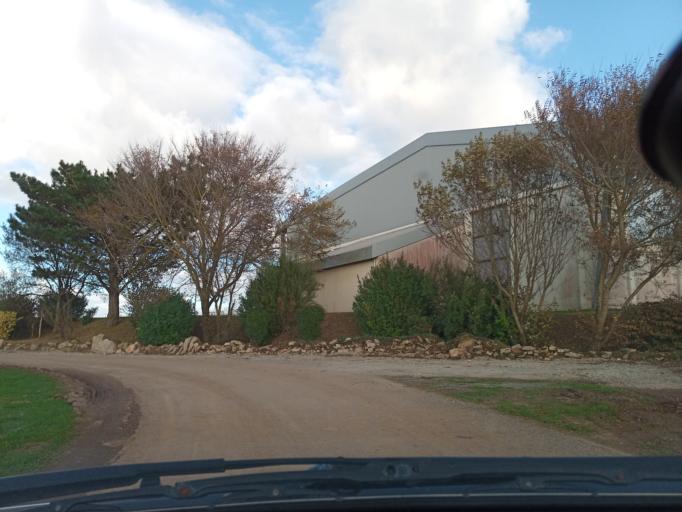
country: FR
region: Brittany
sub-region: Departement du Finistere
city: Plouhinec
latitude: 48.0172
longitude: -4.4930
